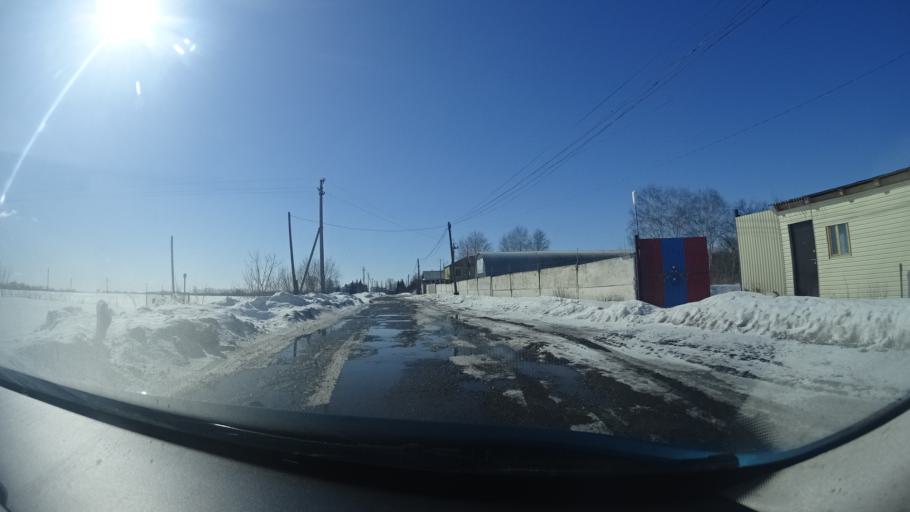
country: RU
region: Bashkortostan
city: Chishmy
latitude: 54.5906
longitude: 55.4123
